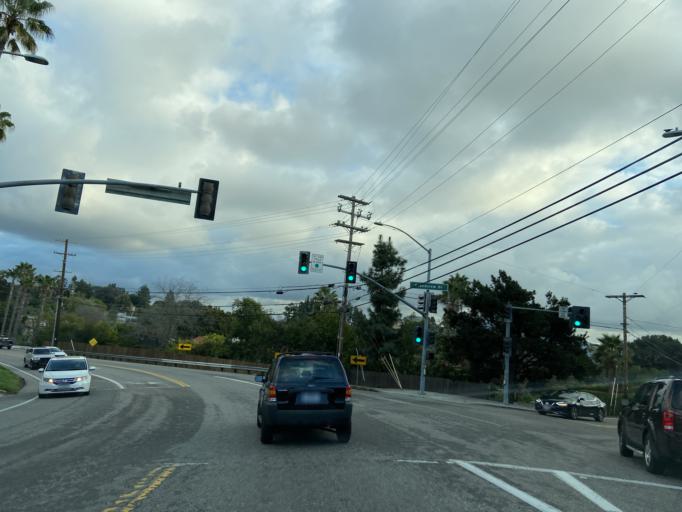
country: US
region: California
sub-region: San Diego County
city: Casa de Oro-Mount Helix
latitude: 32.7663
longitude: -116.9723
